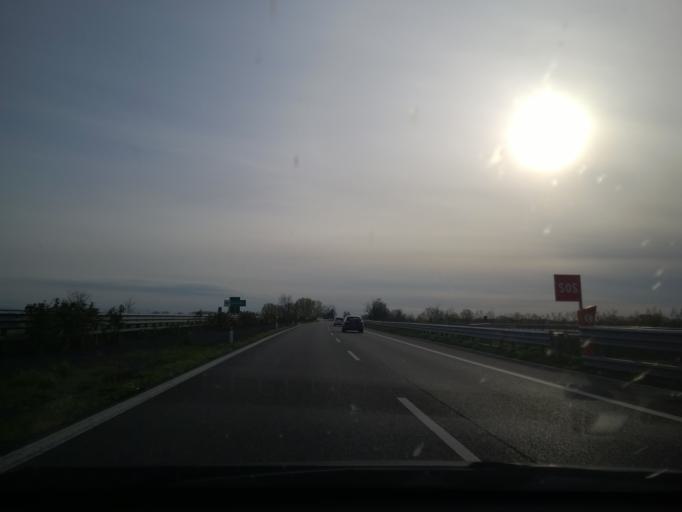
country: IT
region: Lombardy
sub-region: Provincia di Cremona
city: Bosco Ex Parmigiano
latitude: 45.1114
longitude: 10.0514
